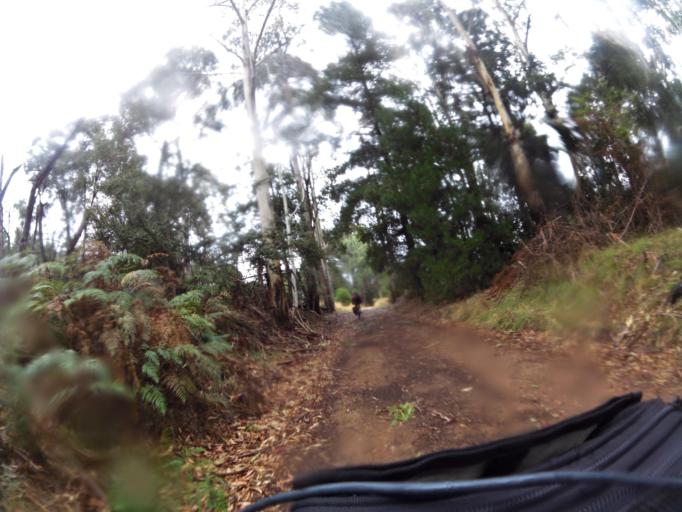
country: AU
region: New South Wales
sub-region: Greater Hume Shire
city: Holbrook
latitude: -36.1931
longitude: 147.5386
